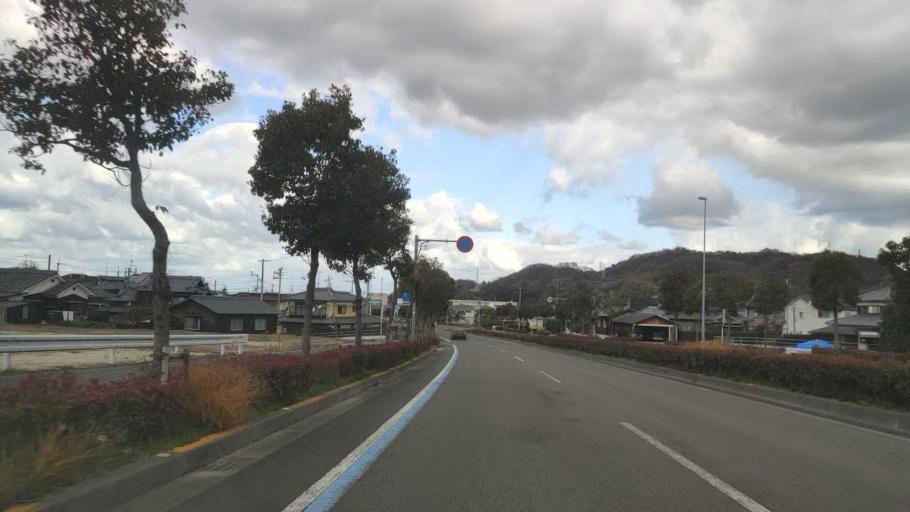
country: JP
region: Ehime
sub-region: Shikoku-chuo Shi
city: Matsuyama
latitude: 33.8960
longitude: 132.7582
